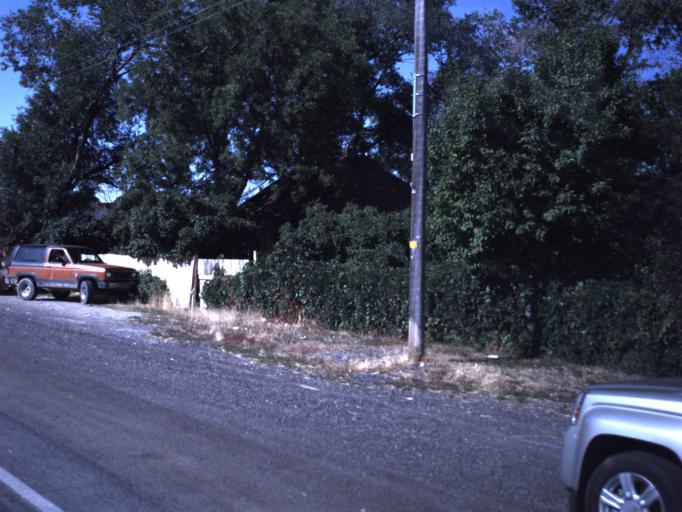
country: US
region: Utah
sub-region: Sanpete County
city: Manti
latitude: 39.1959
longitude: -111.6926
